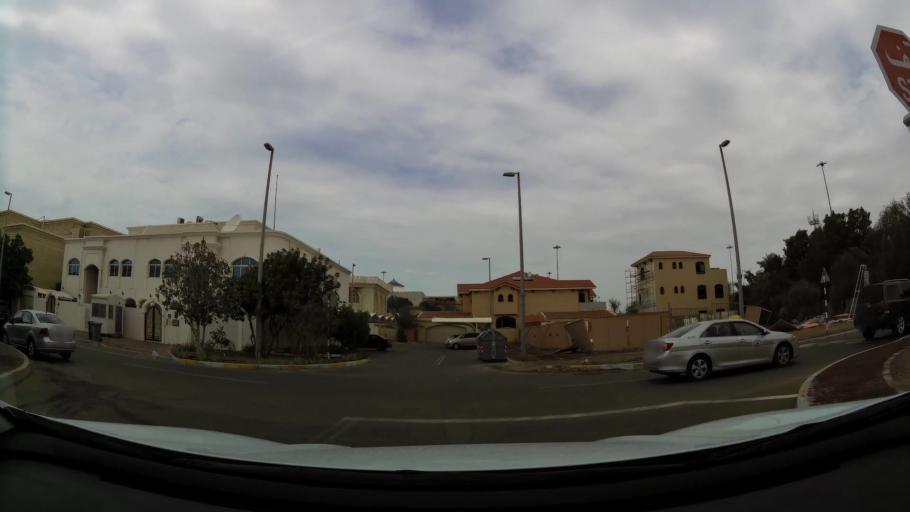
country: AE
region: Abu Dhabi
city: Abu Dhabi
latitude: 24.4315
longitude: 54.4124
